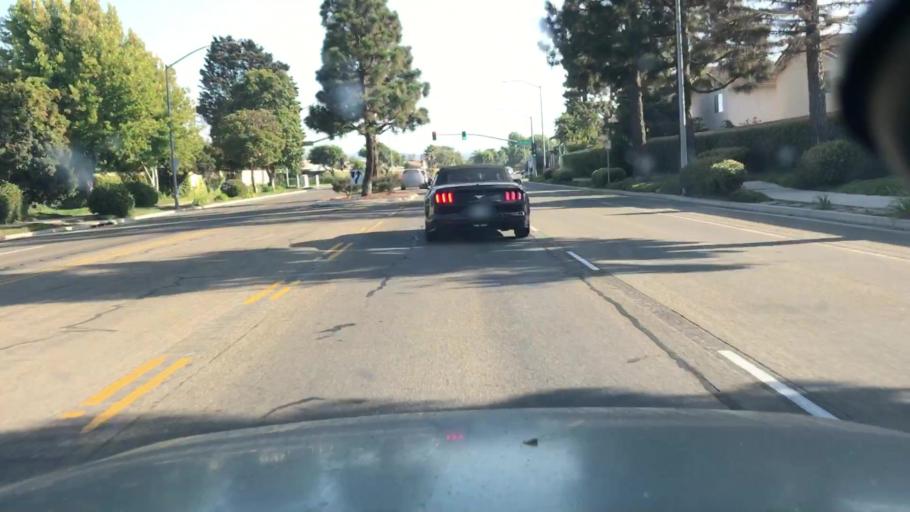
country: US
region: California
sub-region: Santa Barbara County
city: Santa Maria
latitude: 34.9139
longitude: -120.4316
